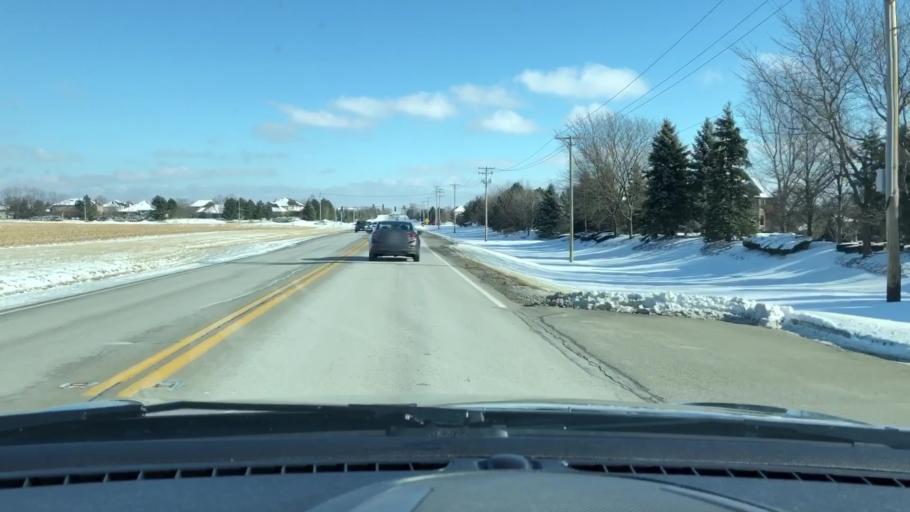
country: US
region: Illinois
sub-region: Will County
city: Mokena
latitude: 41.4838
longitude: -87.9012
